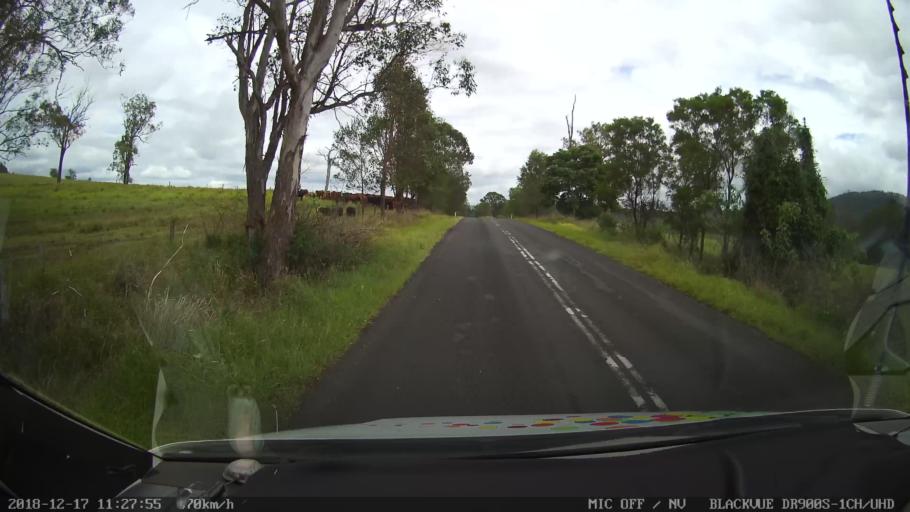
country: AU
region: New South Wales
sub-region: Kyogle
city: Kyogle
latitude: -28.7468
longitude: 152.6415
